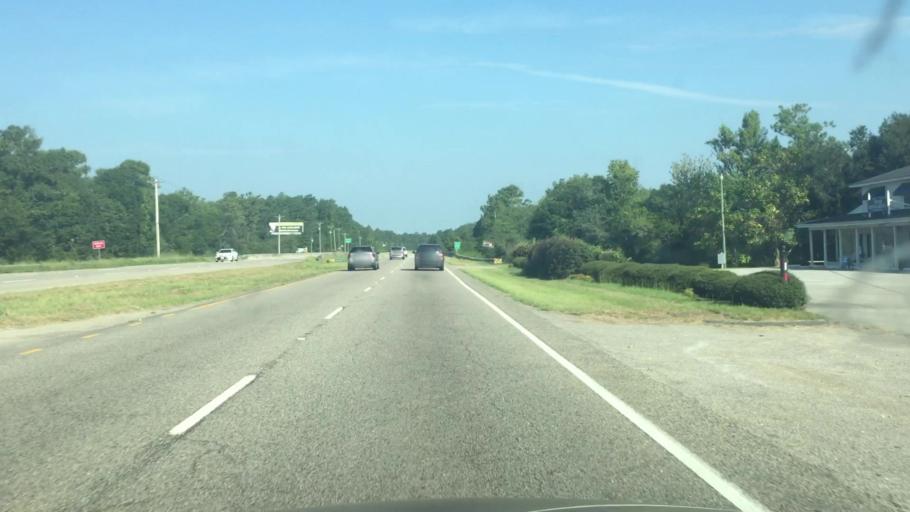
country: US
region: South Carolina
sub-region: Horry County
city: North Myrtle Beach
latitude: 33.9106
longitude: -78.7123
